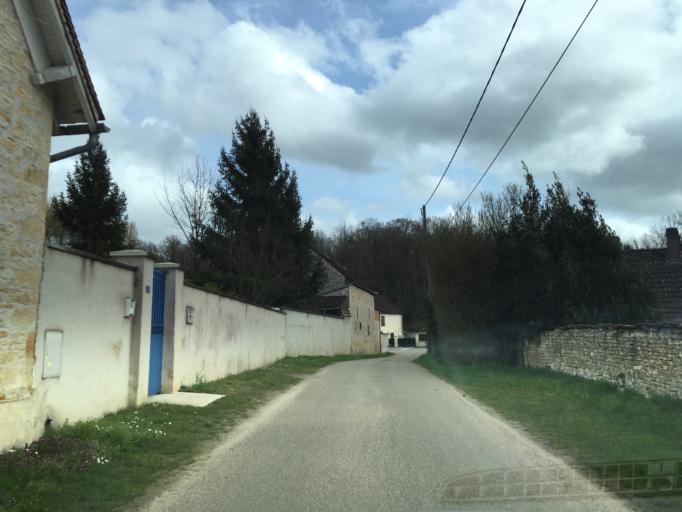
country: FR
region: Bourgogne
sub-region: Departement de l'Yonne
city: Fleury-la-Vallee
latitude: 47.8424
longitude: 3.4031
